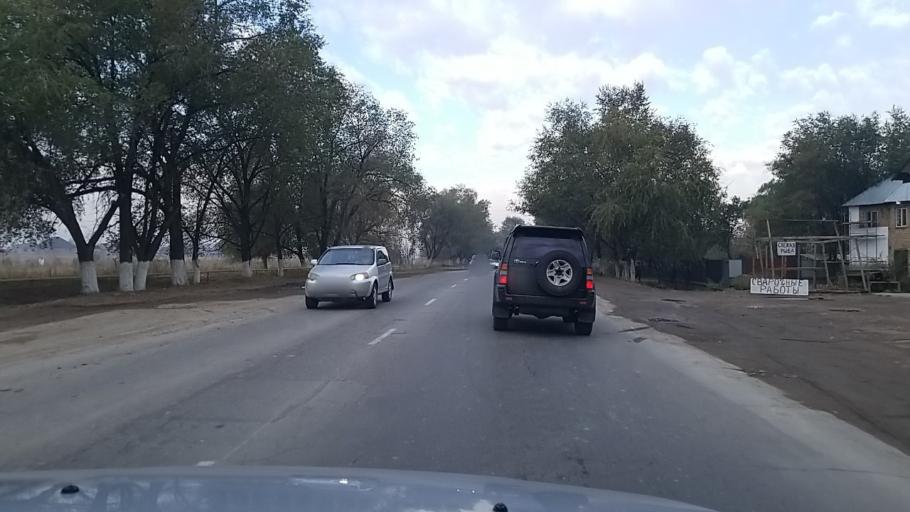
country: KZ
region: Almaty Oblysy
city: Burunday
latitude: 43.3591
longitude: 76.7549
